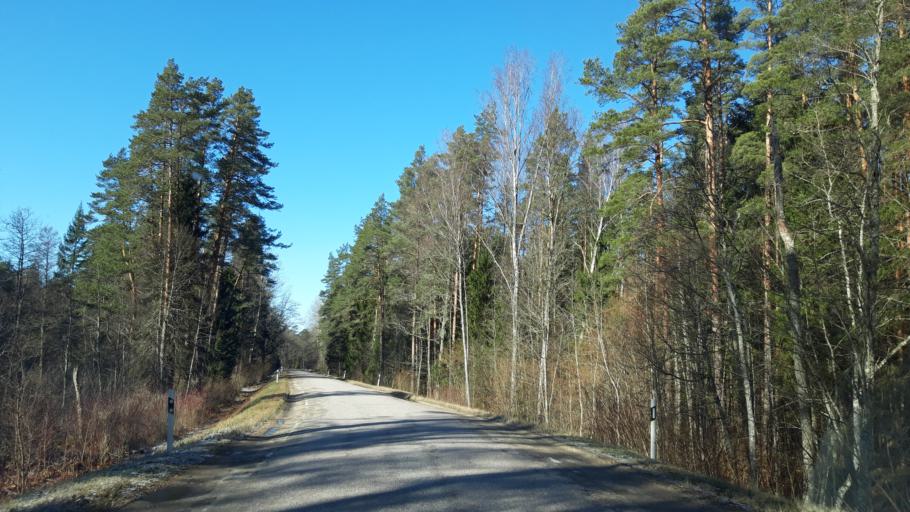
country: LV
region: Strenci
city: Strenci
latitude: 57.6159
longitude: 25.7076
